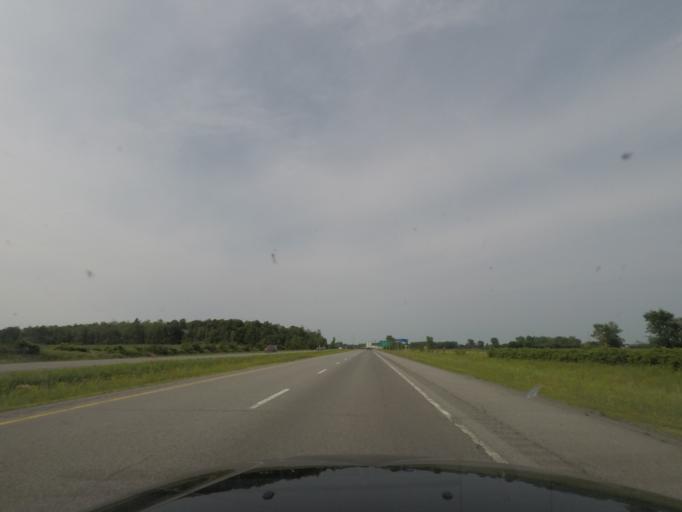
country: CA
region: Quebec
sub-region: Monteregie
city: Napierville
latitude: 45.1838
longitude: -73.4558
